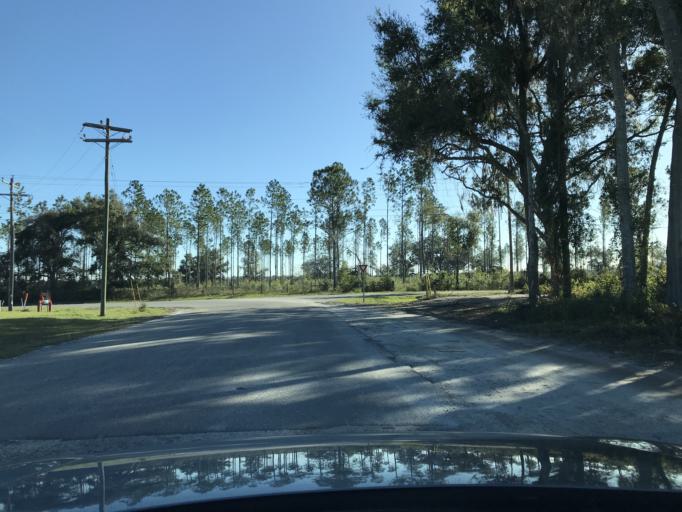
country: US
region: Florida
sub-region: Sumter County
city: Lake Panasoffkee
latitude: 28.7525
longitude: -82.0982
